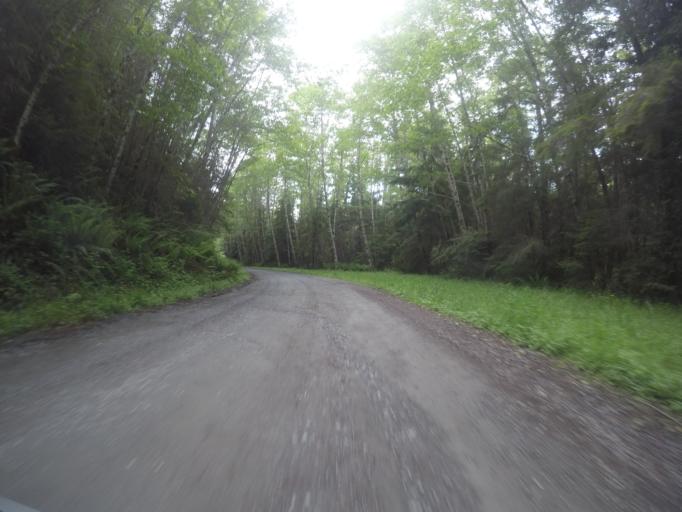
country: US
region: California
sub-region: Humboldt County
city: Westhaven-Moonstone
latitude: 41.2340
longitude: -123.9900
